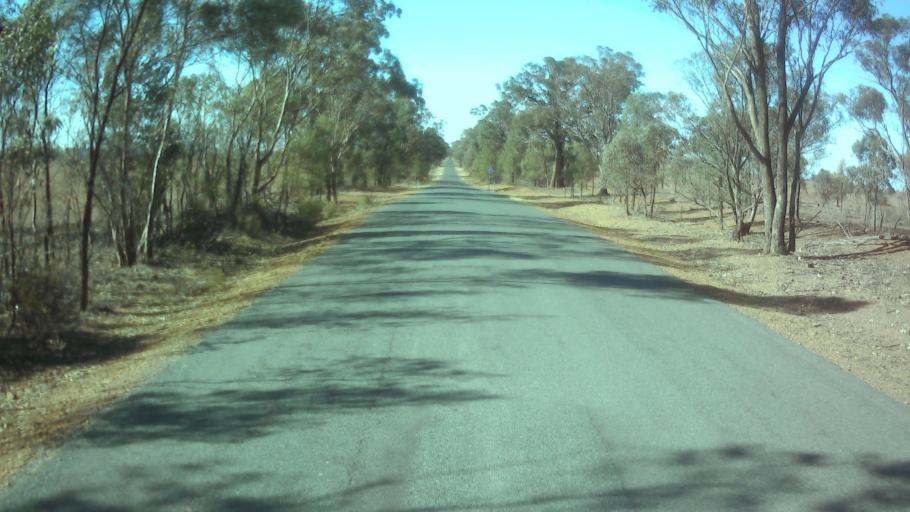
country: AU
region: New South Wales
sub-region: Forbes
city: Forbes
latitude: -33.7044
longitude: 147.8059
